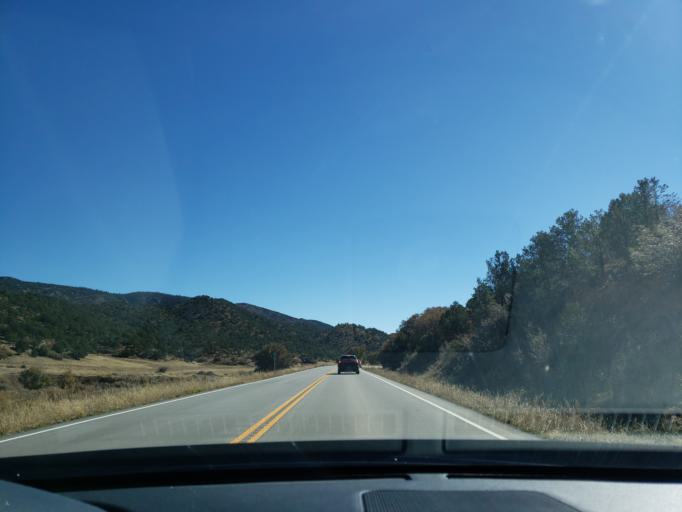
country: US
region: Colorado
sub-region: Fremont County
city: Canon City
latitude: 38.6030
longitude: -105.4325
